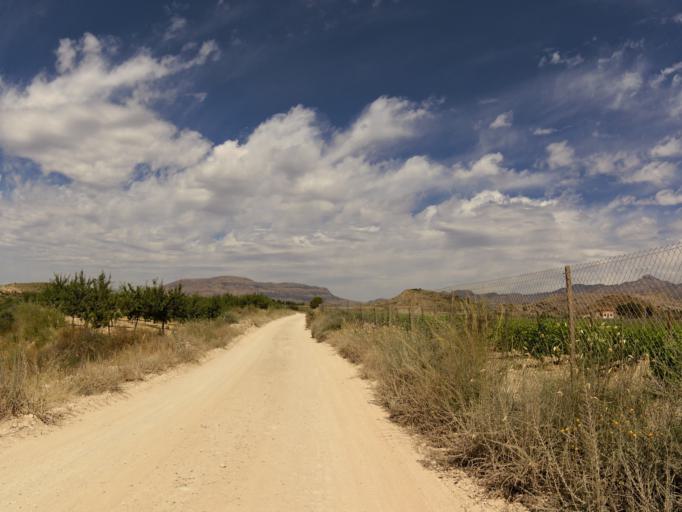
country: ES
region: Valencia
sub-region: Provincia de Alicante
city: Agost
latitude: 38.4045
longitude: -0.6120
